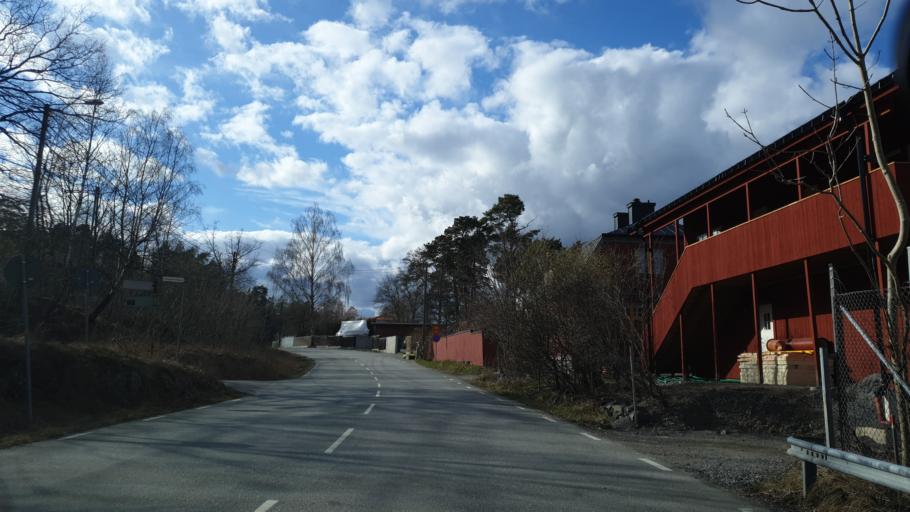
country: SE
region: Stockholm
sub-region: Nacka Kommun
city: Alta
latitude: 59.2986
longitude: 18.2097
